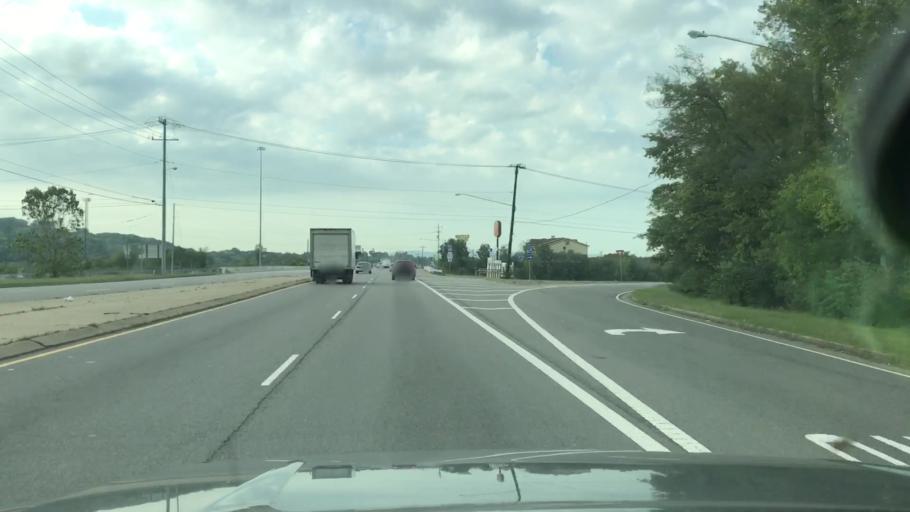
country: US
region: Tennessee
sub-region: Davidson County
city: Nashville
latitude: 36.2394
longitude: -86.7577
